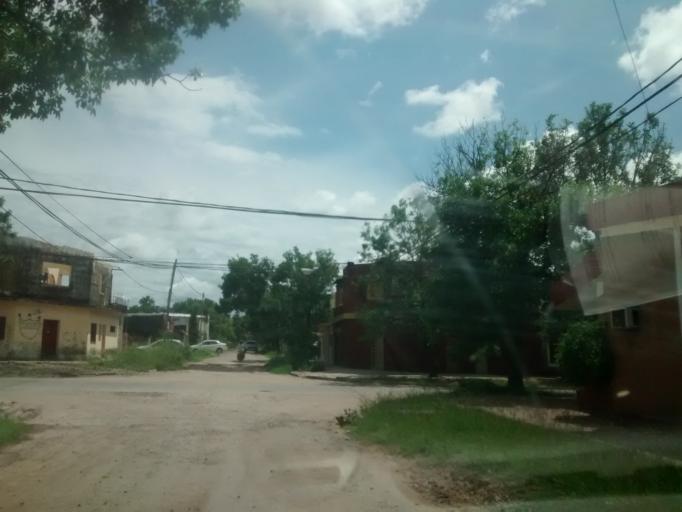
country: AR
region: Chaco
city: Resistencia
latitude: -27.4497
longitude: -59.0008
